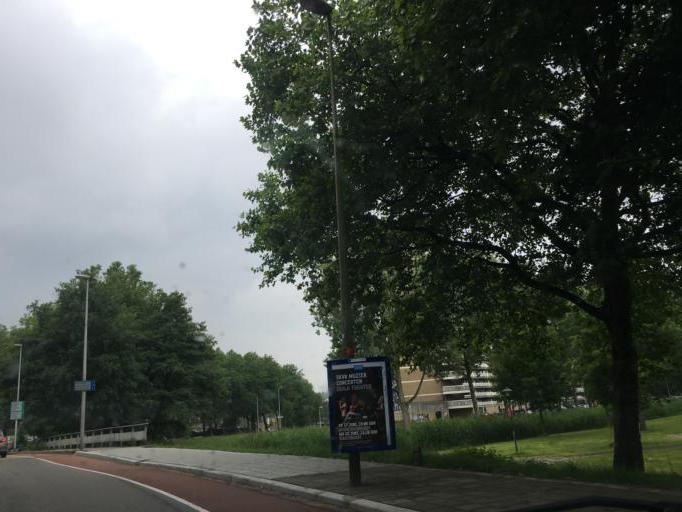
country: NL
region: South Holland
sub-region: Gemeente Krimpen aan den IJssel
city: Krimpen aan den IJssel
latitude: 51.9405
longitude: 4.6002
